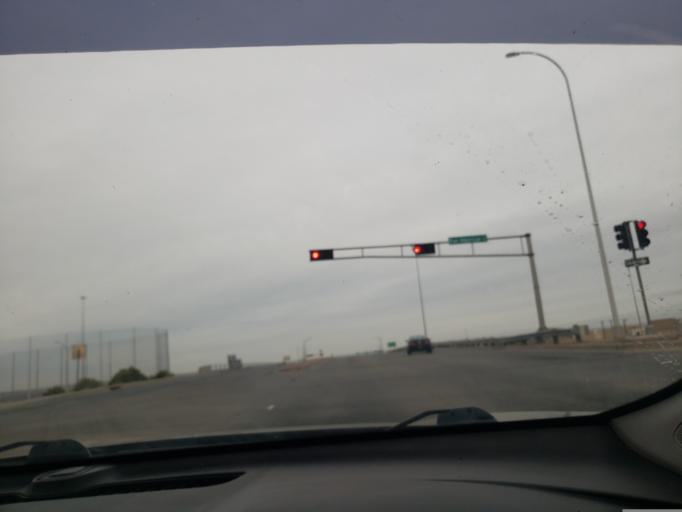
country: US
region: New Mexico
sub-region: Bernalillo County
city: Lee Acres
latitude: 35.1323
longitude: -106.6088
